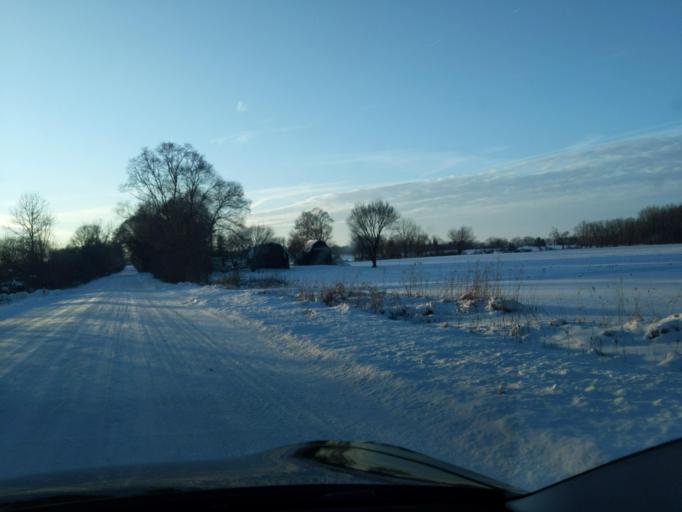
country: US
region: Michigan
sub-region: Ingham County
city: Webberville
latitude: 42.5679
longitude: -84.1338
